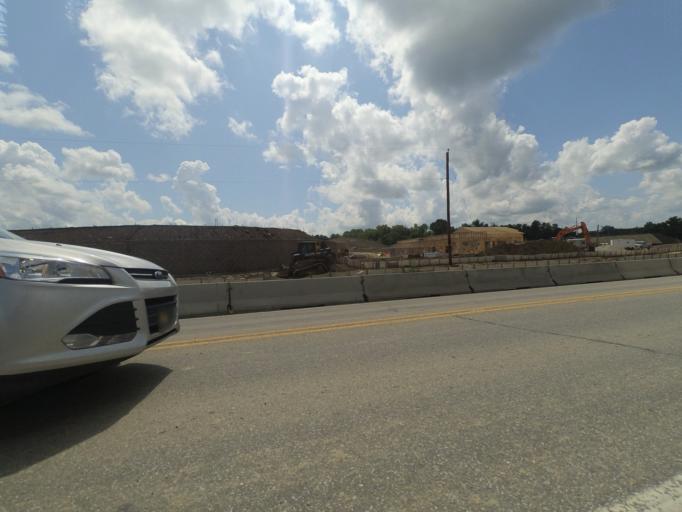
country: US
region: West Virginia
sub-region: Cabell County
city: Barboursville
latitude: 38.4149
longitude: -82.2885
